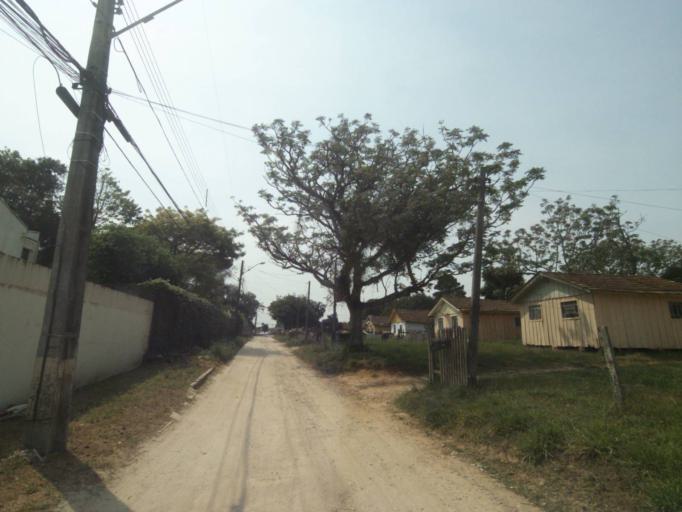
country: BR
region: Parana
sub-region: Pinhais
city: Pinhais
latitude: -25.4836
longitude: -49.2154
